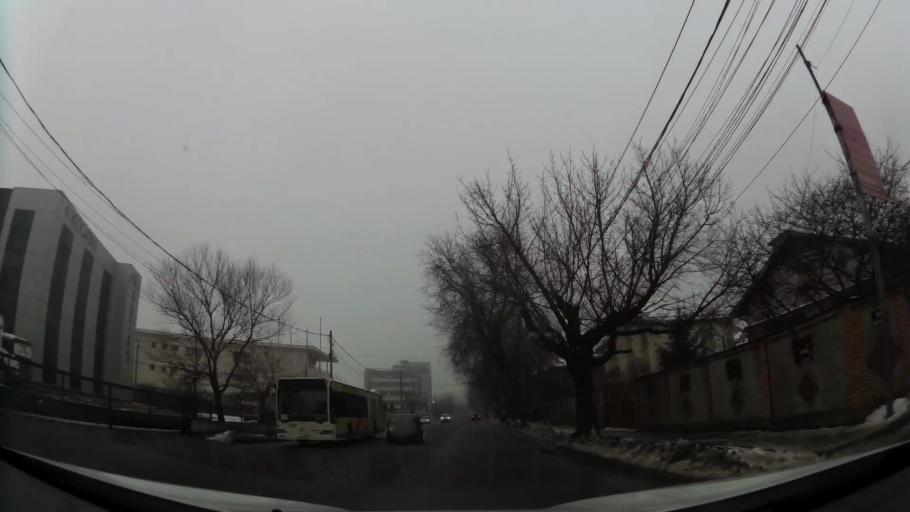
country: RO
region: Ilfov
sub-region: Comuna Chiajna
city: Rosu
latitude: 44.4446
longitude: 26.0186
